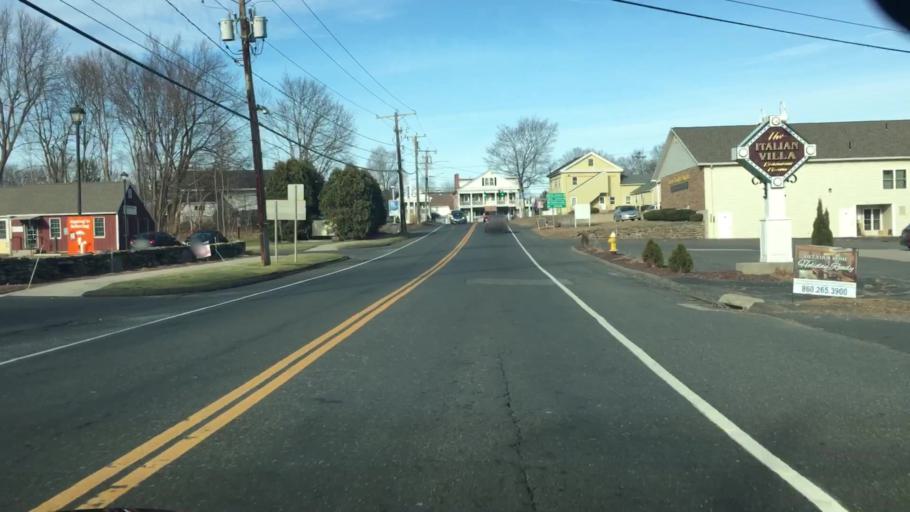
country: US
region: Connecticut
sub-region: Tolland County
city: Somers
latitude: 41.9841
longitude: -72.4475
